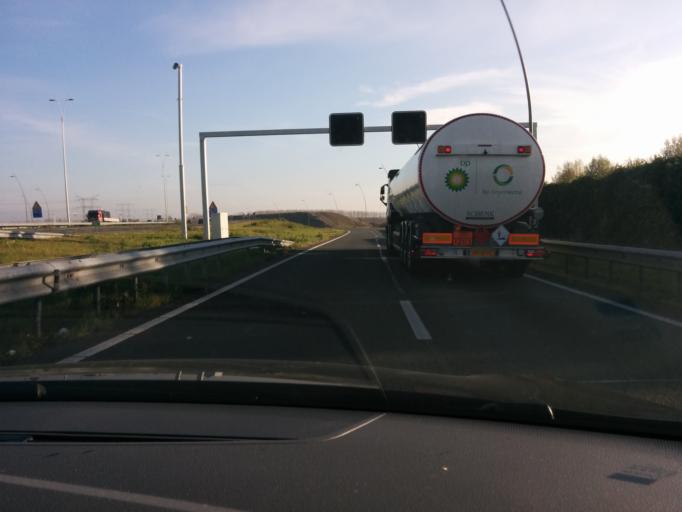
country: NL
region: North Brabant
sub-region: Gemeente Son en Breugel
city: Son
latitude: 51.4959
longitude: 5.4682
